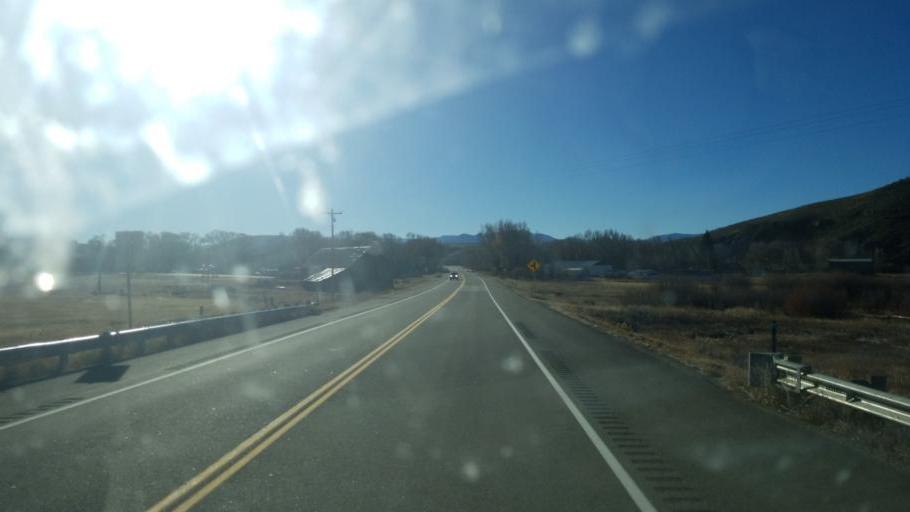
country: US
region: Colorado
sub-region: Gunnison County
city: Gunnison
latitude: 38.5047
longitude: -106.7303
